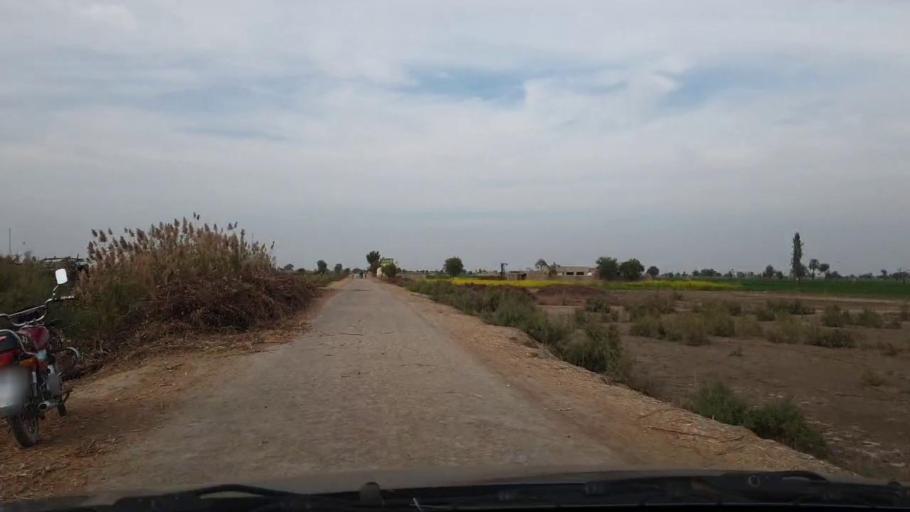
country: PK
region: Sindh
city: Khadro
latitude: 26.1594
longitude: 68.7304
